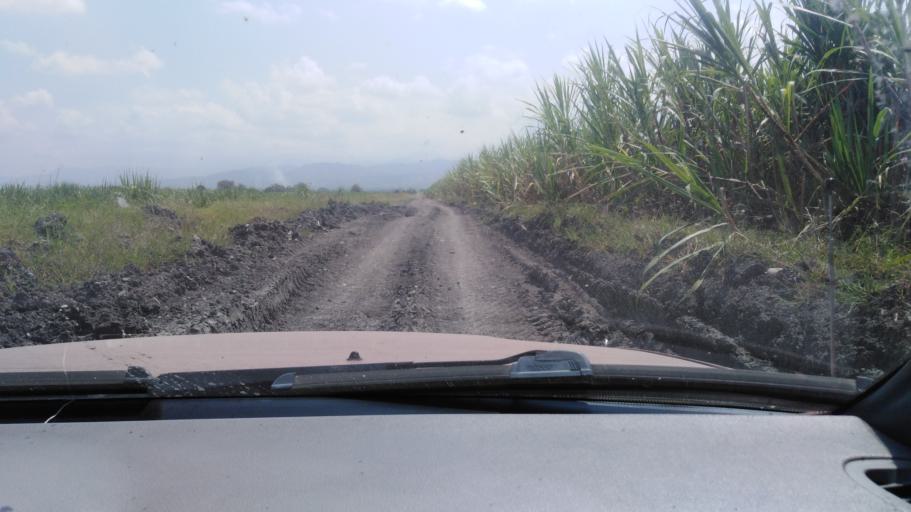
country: CO
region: Valle del Cauca
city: San Pedro
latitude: 3.9998
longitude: -76.2850
